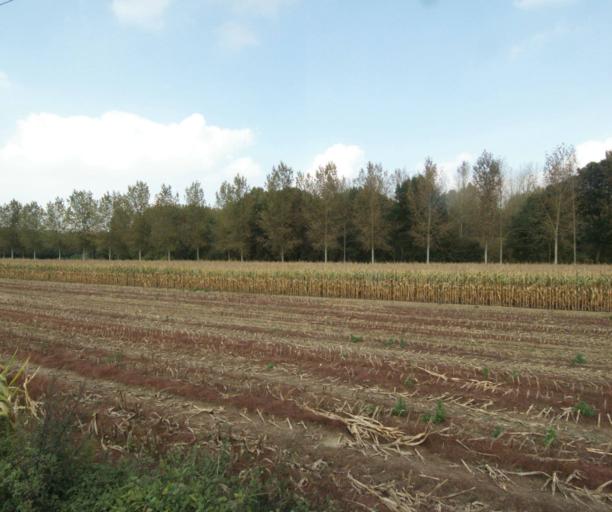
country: FR
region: Nord-Pas-de-Calais
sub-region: Departement du Nord
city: Emmerin
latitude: 50.5812
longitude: 2.9921
